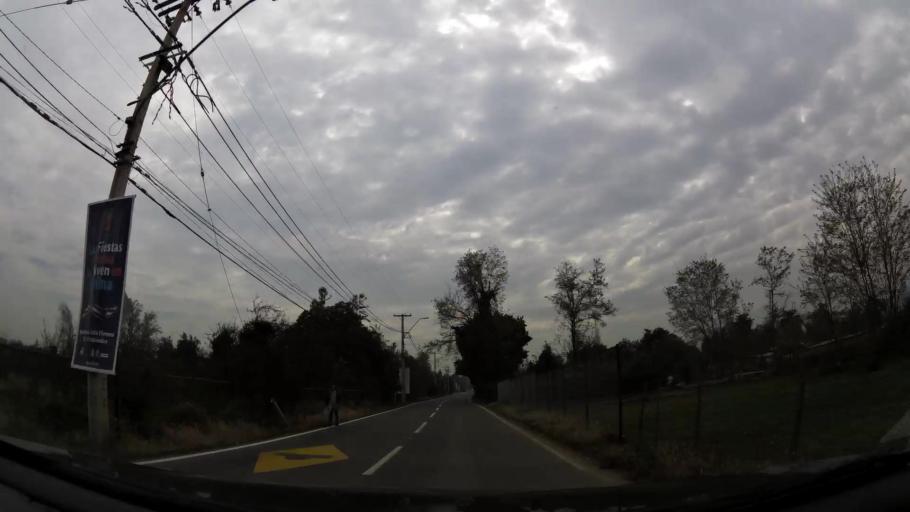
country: CL
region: Santiago Metropolitan
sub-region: Provincia de Chacabuco
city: Chicureo Abajo
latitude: -33.2125
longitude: -70.6620
